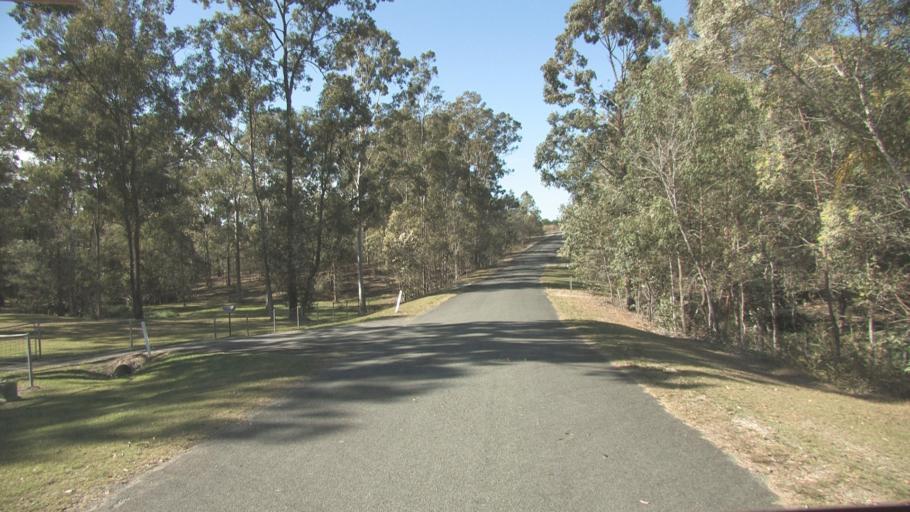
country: AU
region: Queensland
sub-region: Ipswich
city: Springfield Lakes
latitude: -27.7163
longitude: 152.9290
